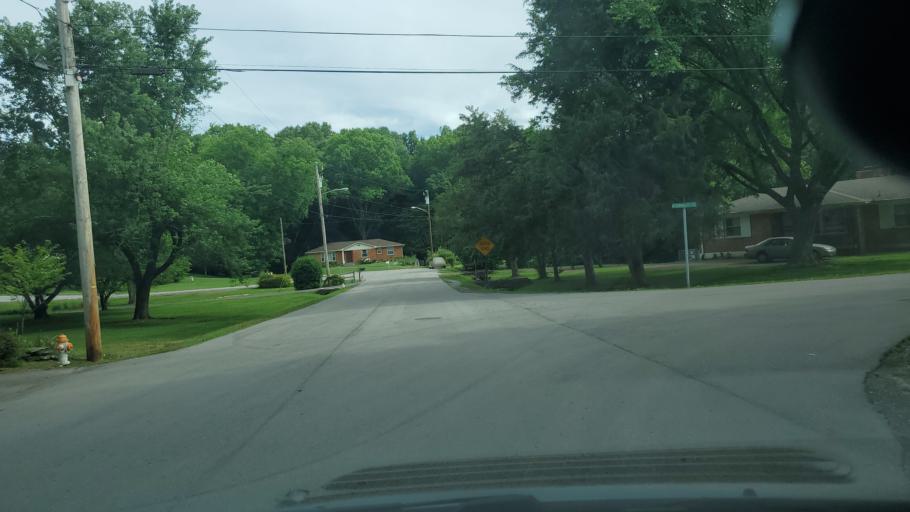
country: US
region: Tennessee
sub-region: Davidson County
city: Lakewood
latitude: 36.2219
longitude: -86.6838
